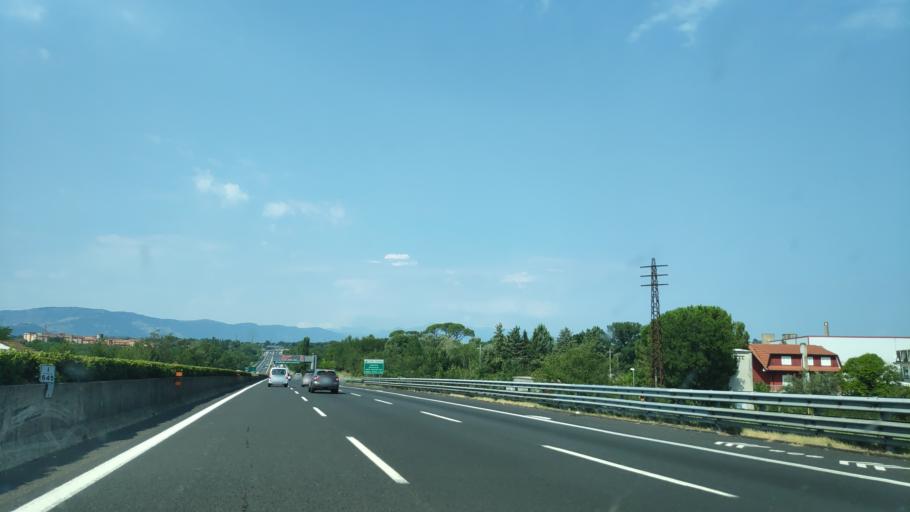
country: IT
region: Latium
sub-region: Provincia di Frosinone
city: Ceprano
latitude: 41.5433
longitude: 13.5265
